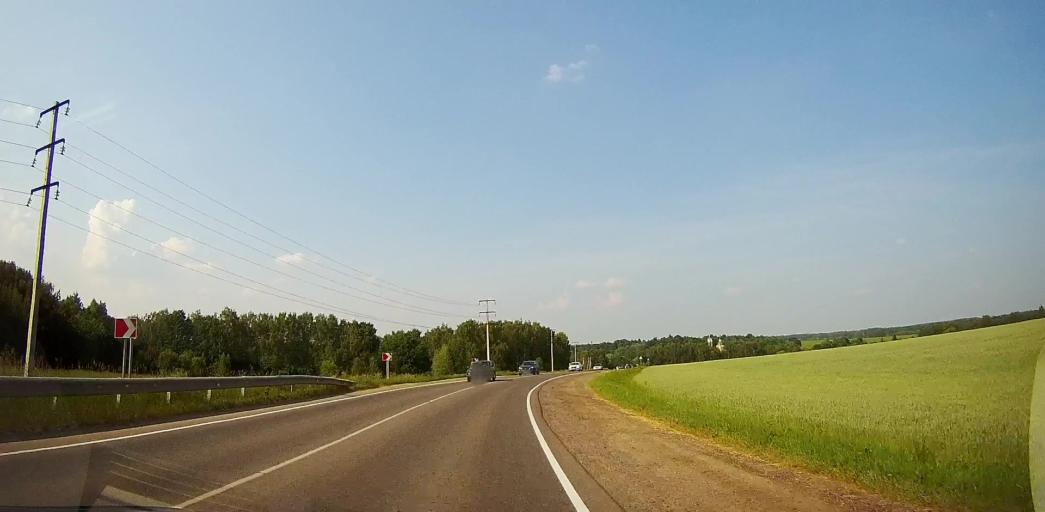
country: RU
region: Moskovskaya
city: Barybino
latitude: 55.2887
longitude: 37.9121
